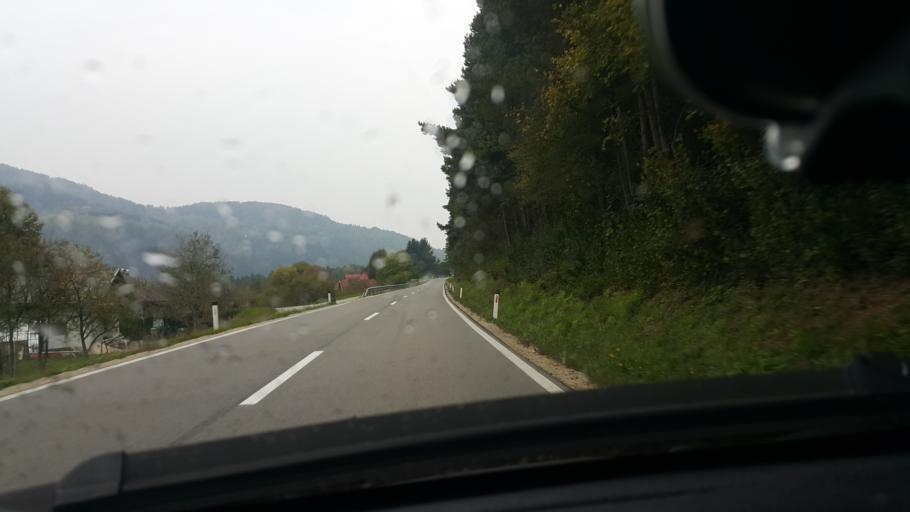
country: SI
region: Dravograd
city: Dravograd
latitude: 46.5969
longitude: 14.9993
